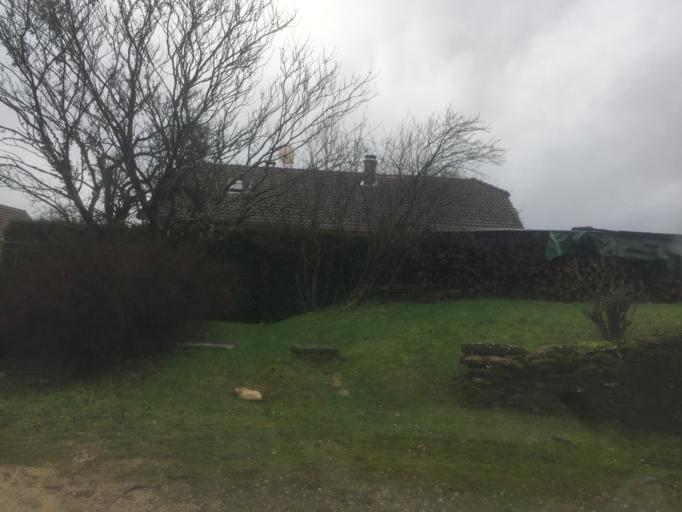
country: FR
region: Franche-Comte
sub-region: Departement du Jura
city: Dampierre
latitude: 47.2077
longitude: 5.7090
